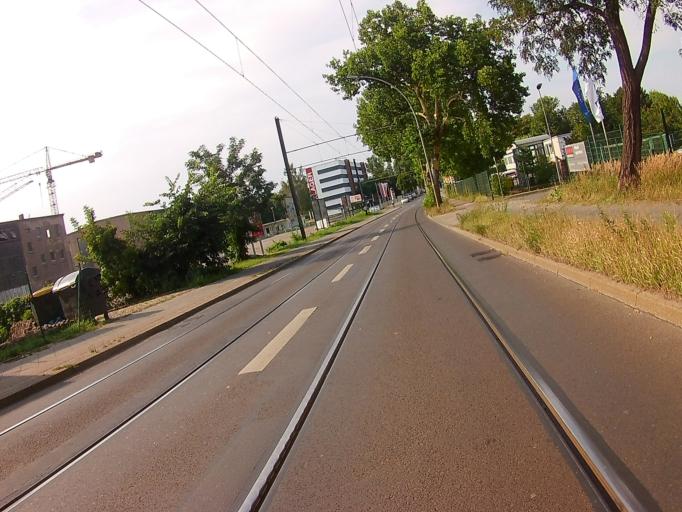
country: DE
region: Berlin
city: Grunau
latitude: 52.4290
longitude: 13.5723
